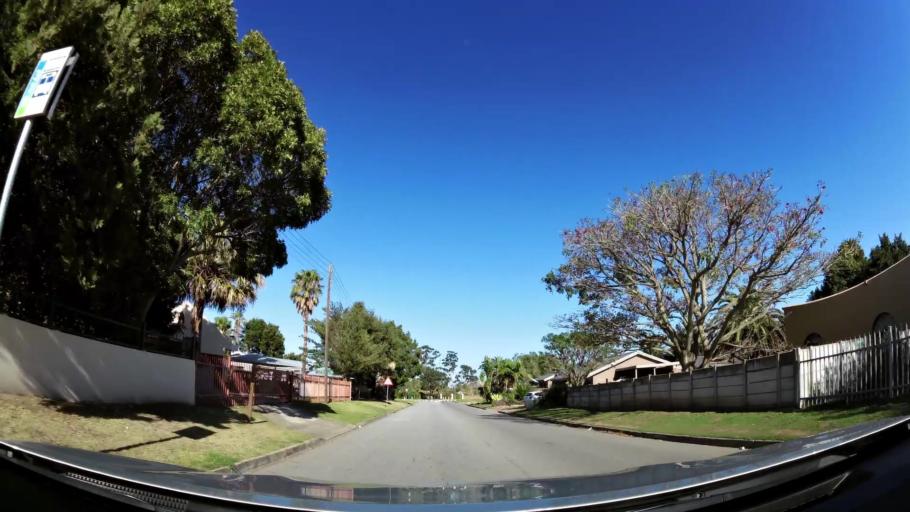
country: ZA
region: Western Cape
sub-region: Eden District Municipality
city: George
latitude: -33.9490
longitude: 22.4152
